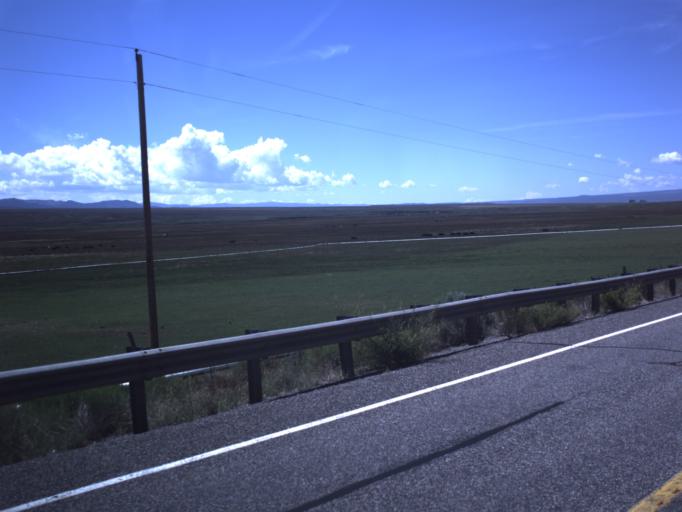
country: US
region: Utah
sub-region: Garfield County
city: Panguitch
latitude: 38.0066
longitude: -112.3793
